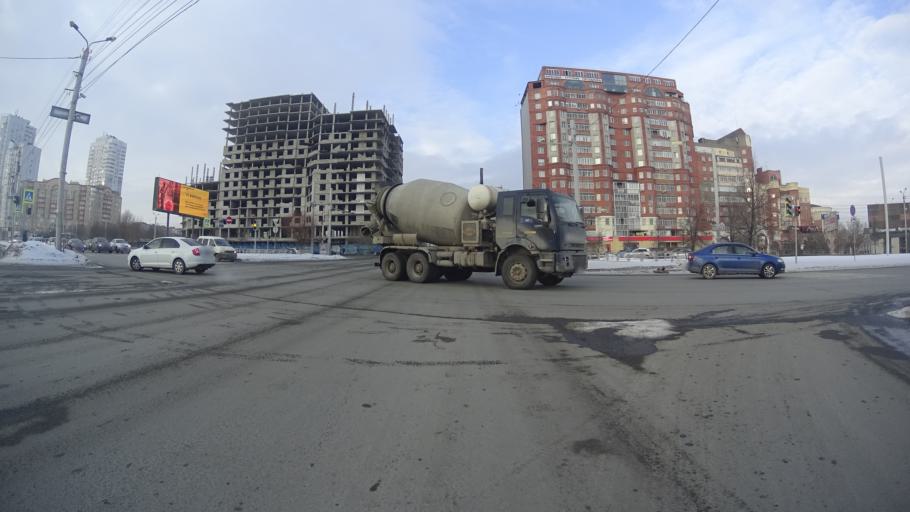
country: RU
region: Chelyabinsk
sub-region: Gorod Chelyabinsk
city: Chelyabinsk
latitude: 55.1736
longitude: 61.3950
